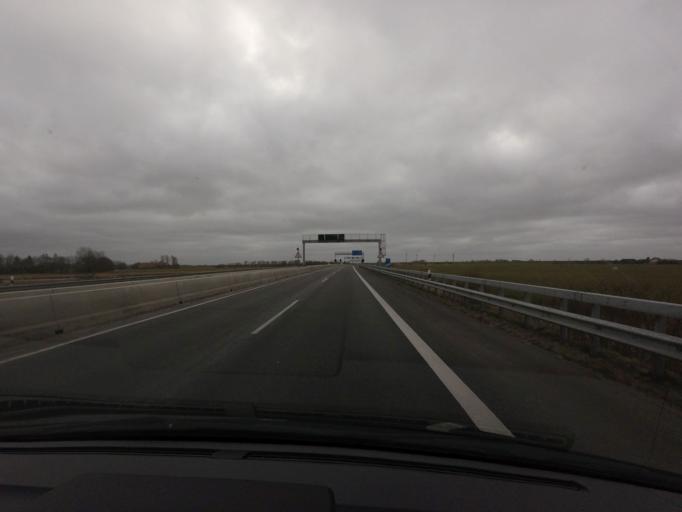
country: DE
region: Lower Saxony
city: Jemgum
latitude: 53.2414
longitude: 7.4176
